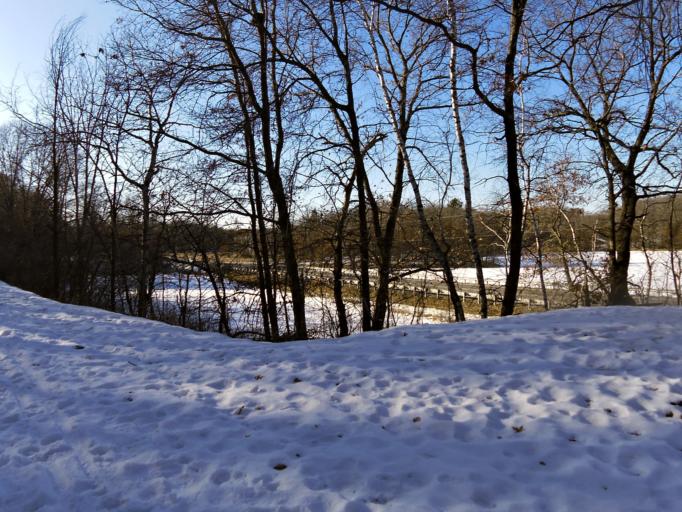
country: US
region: Minnesota
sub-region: Washington County
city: Grant
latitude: 45.0790
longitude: -92.8861
